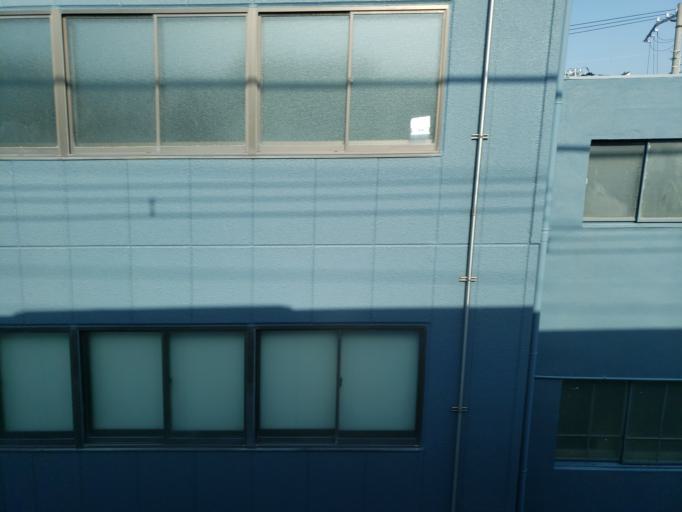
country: JP
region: Hyogo
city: Kobe
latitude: 34.6644
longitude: 135.1578
